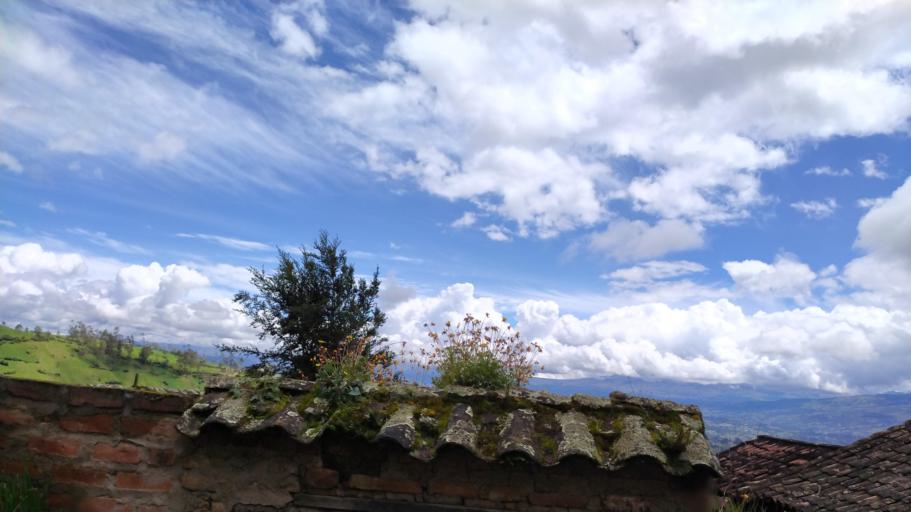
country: EC
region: Chimborazo
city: Riobamba
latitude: -1.6850
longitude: -78.5755
